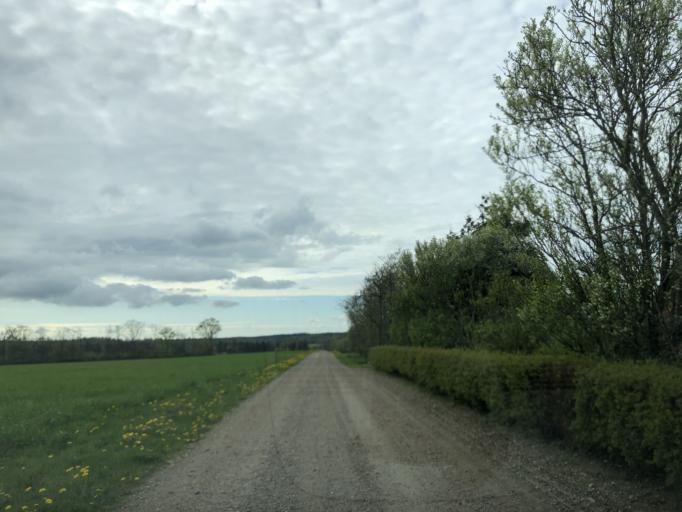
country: DK
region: Central Jutland
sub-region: Holstebro Kommune
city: Ulfborg
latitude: 56.1922
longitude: 8.4708
